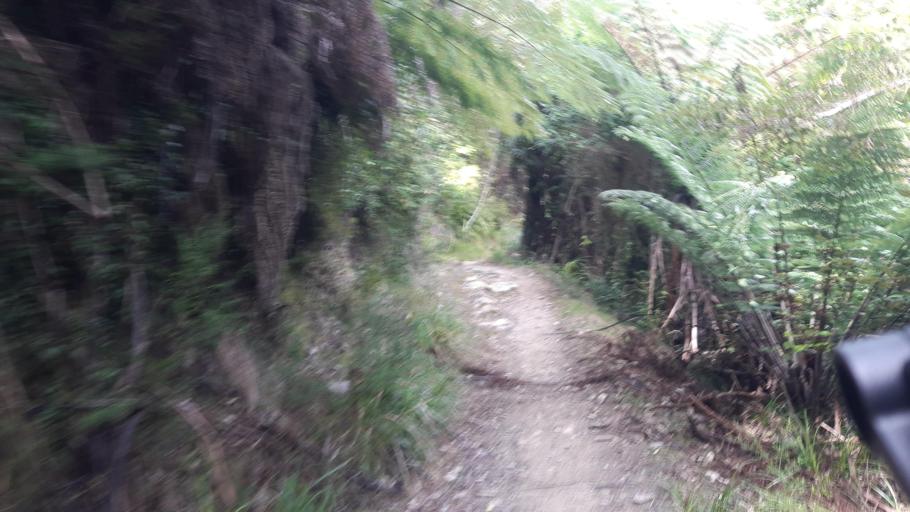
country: NZ
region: Marlborough
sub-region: Marlborough District
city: Picton
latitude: -41.2488
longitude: 173.9597
